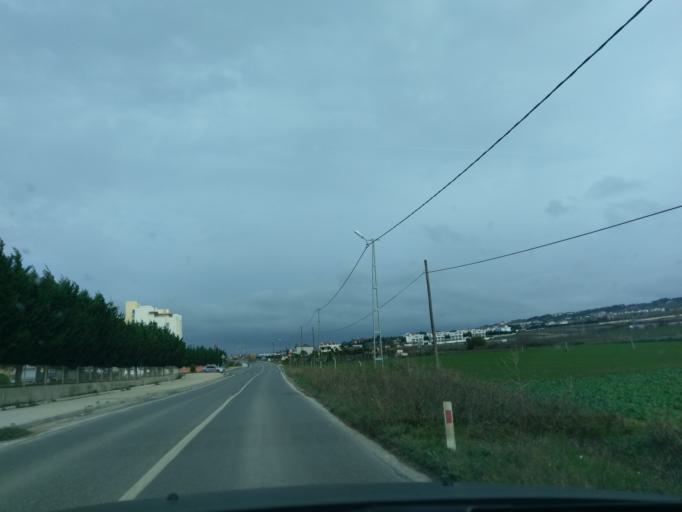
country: TR
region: Istanbul
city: Selimpasa
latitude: 41.0751
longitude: 28.3711
